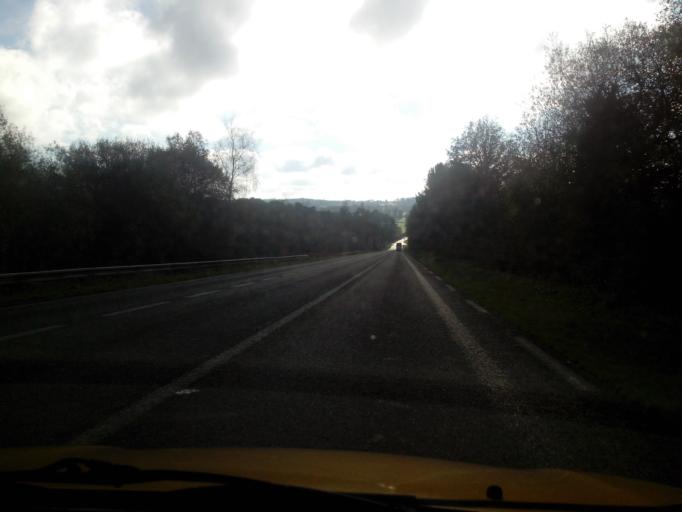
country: FR
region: Brittany
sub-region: Departement du Morbihan
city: Molac
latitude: 47.7273
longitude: -2.4411
